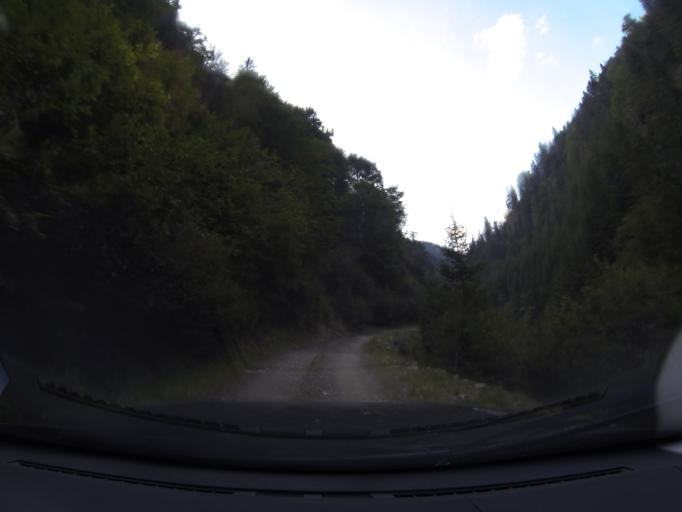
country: RO
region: Arges
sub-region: Comuna Arefu
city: Arefu
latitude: 45.5228
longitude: 24.6777
